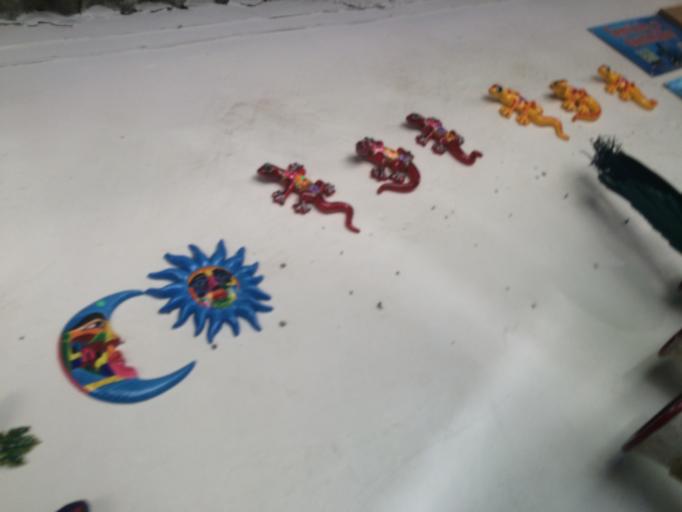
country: MX
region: Colima
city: Suchitlan
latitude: 19.3746
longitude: -103.7087
